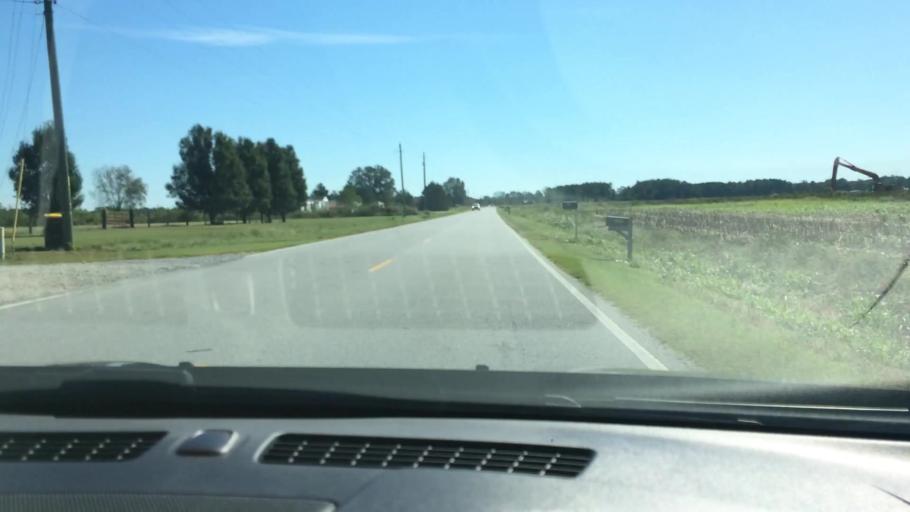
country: US
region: North Carolina
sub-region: Pitt County
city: Grifton
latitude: 35.3857
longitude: -77.3794
